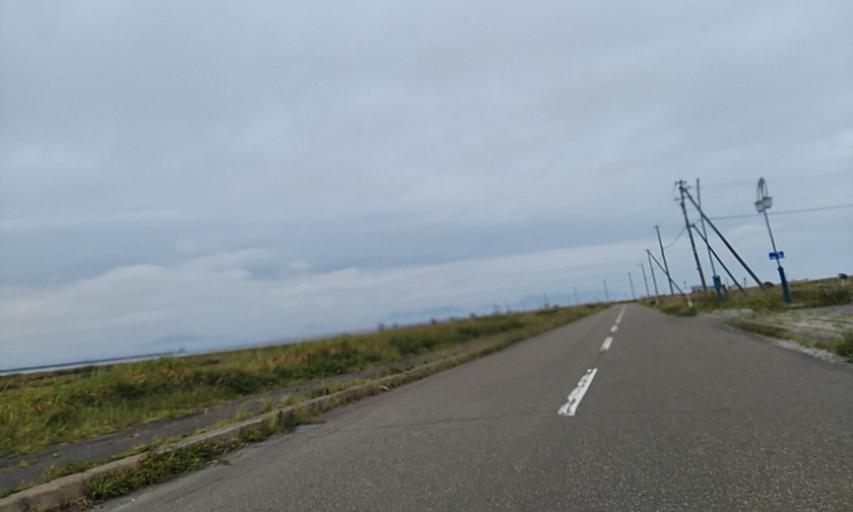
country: JP
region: Hokkaido
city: Shibetsu
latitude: 43.5676
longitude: 145.3465
